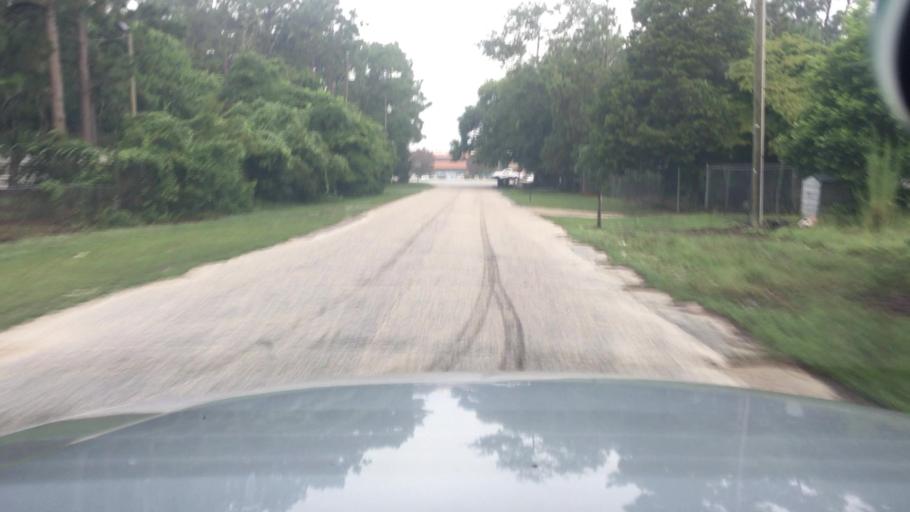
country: US
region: North Carolina
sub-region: Cumberland County
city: Hope Mills
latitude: 35.0134
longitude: -78.9173
